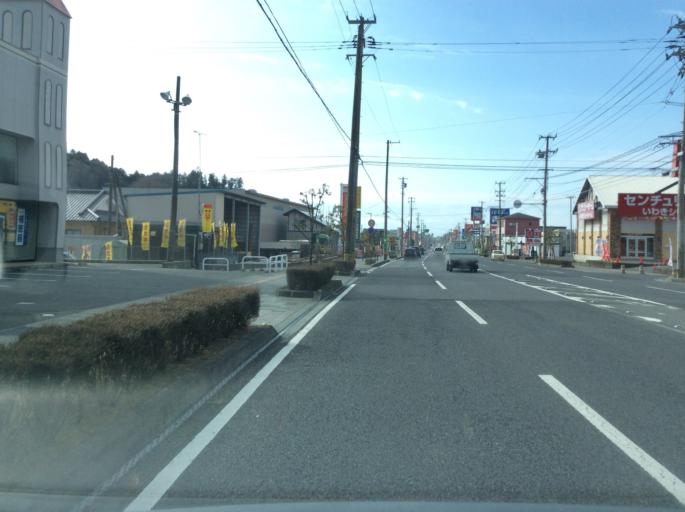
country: JP
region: Fukushima
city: Iwaki
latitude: 36.9693
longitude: 140.9052
